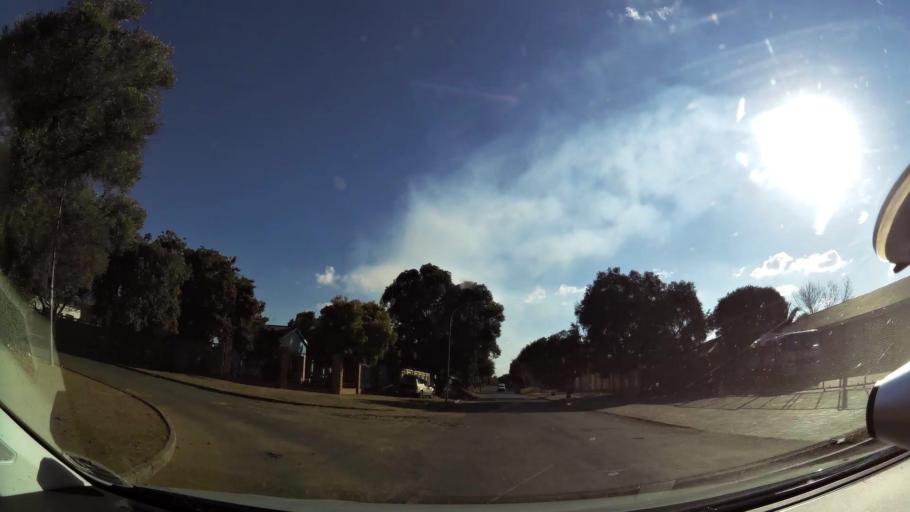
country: ZA
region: Northern Cape
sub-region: Frances Baard District Municipality
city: Kimberley
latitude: -28.7482
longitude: 24.7600
